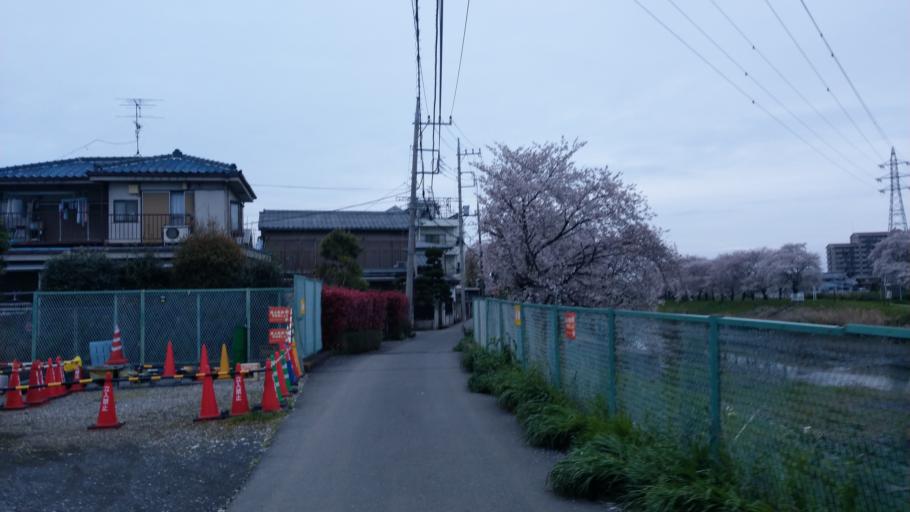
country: JP
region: Saitama
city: Yono
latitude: 35.8945
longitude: 139.5960
